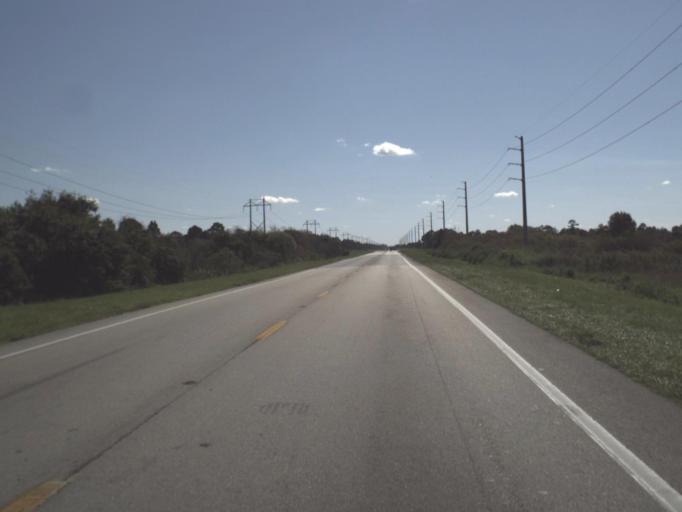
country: US
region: Florida
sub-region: Lee County
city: Gateway
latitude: 26.5780
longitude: -81.7051
